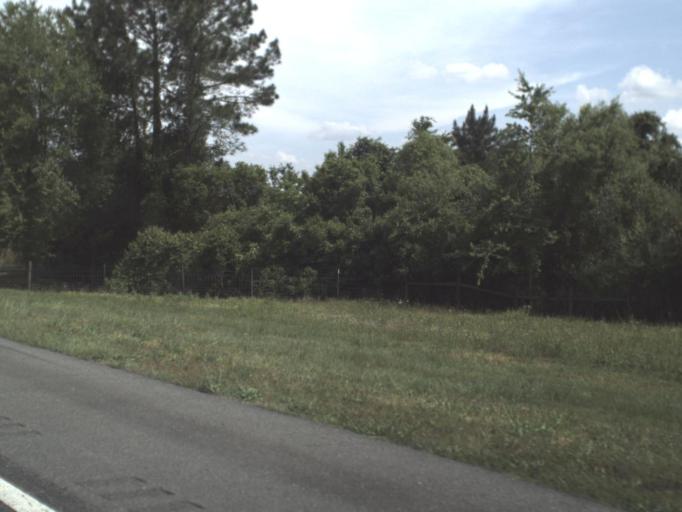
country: US
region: Florida
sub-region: Suwannee County
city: Wellborn
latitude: 30.2816
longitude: -82.8238
